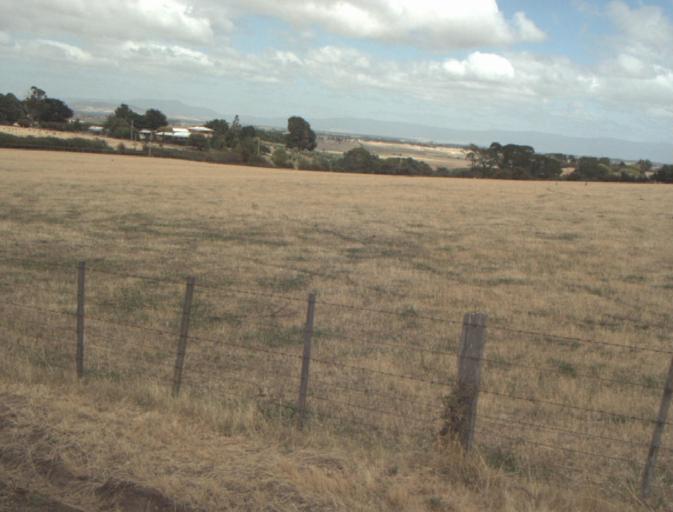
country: AU
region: Tasmania
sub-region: Northern Midlands
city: Evandale
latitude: -41.5214
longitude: 147.2827
